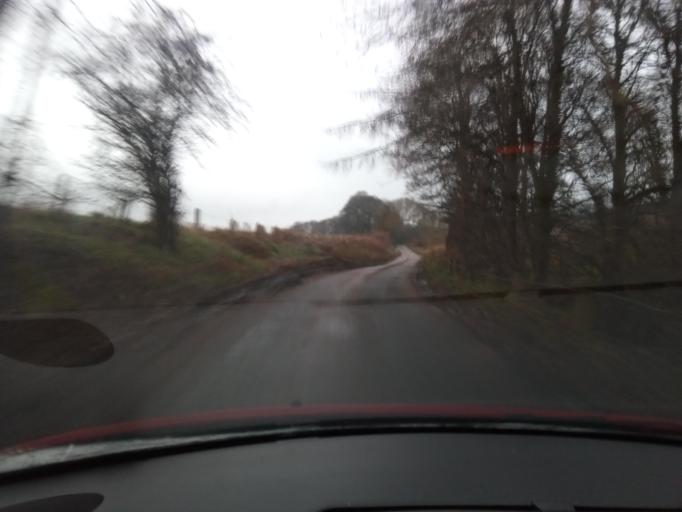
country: GB
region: Scotland
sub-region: The Scottish Borders
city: Kelso
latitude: 55.5434
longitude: -2.4366
